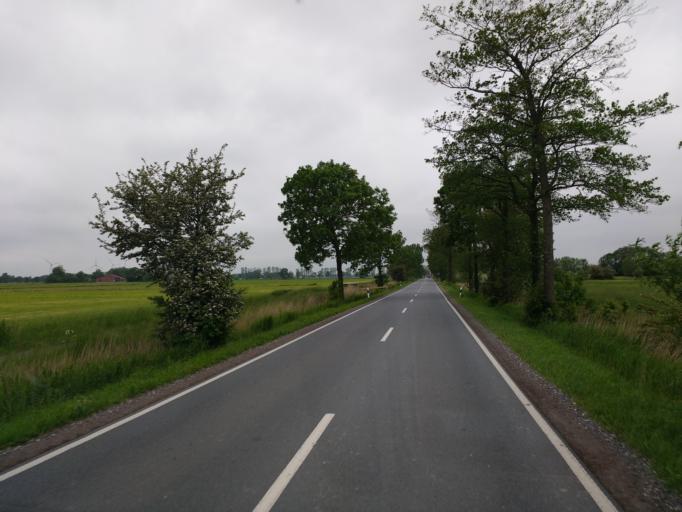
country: DE
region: Lower Saxony
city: Sillenstede
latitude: 53.6107
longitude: 7.9421
